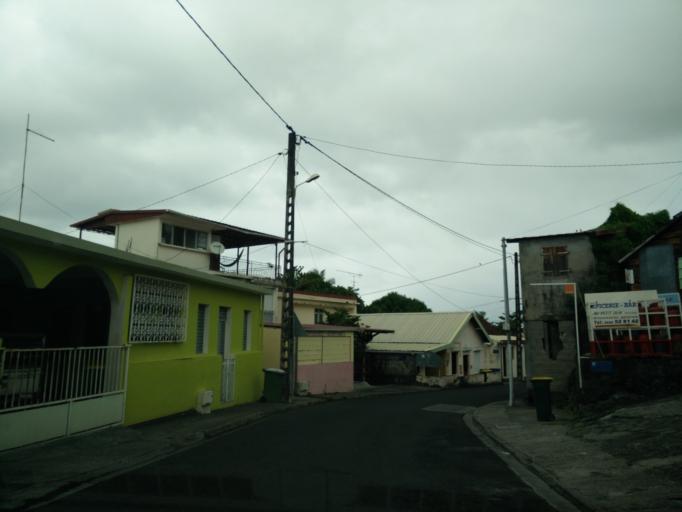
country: MQ
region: Martinique
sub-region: Martinique
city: Saint-Pierre
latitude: 14.8039
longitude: -61.2262
